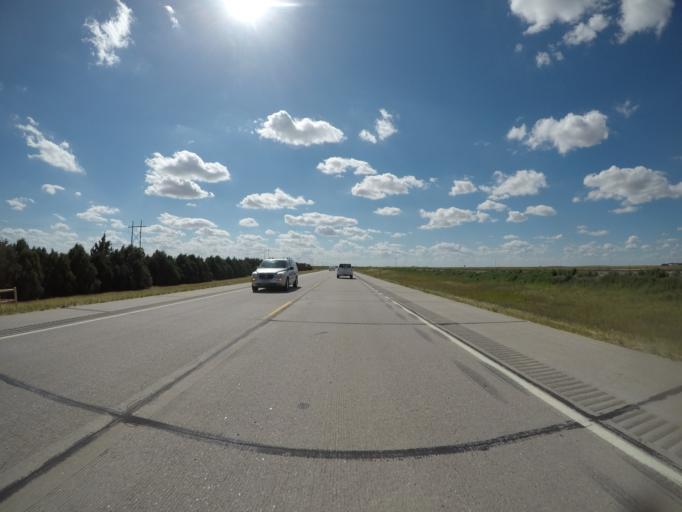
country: US
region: Colorado
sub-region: Phillips County
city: Holyoke
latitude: 40.5996
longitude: -102.3952
